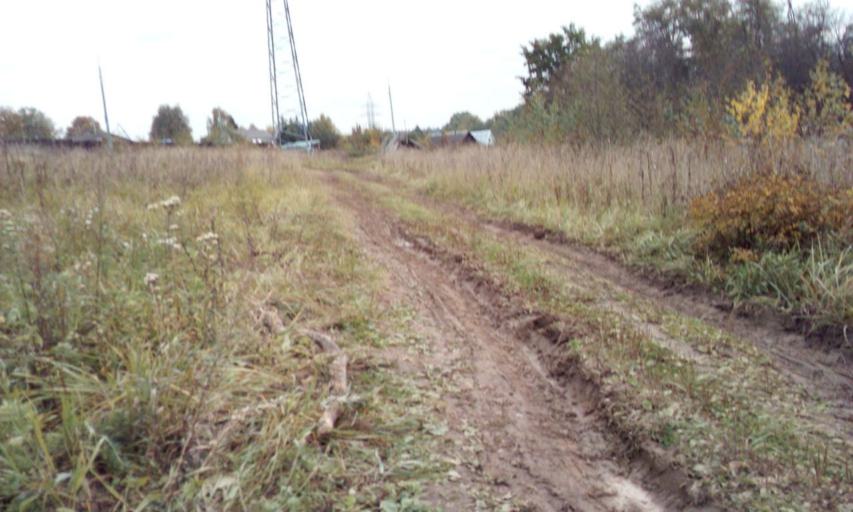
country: RU
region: Moskovskaya
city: Gorki Vtoryye
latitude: 55.6933
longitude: 37.2018
